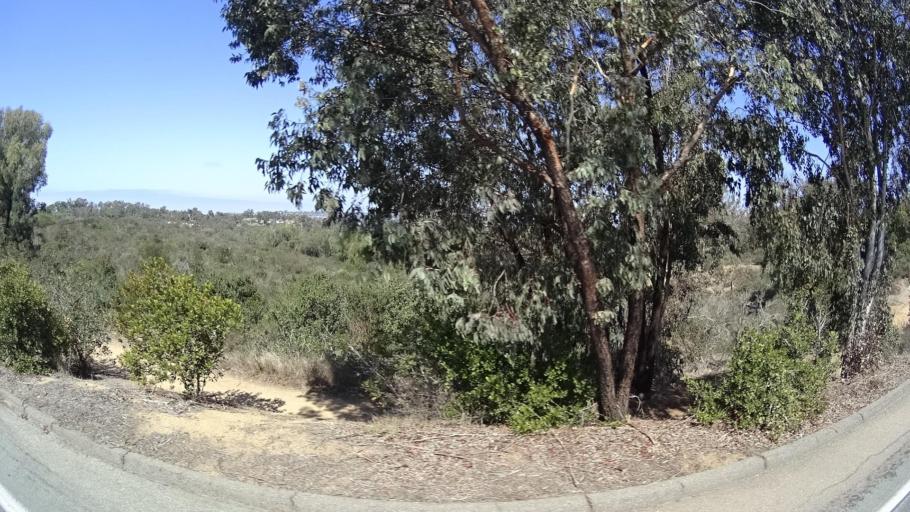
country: US
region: California
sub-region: San Diego County
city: Rancho Santa Fe
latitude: 32.9960
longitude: -117.2299
